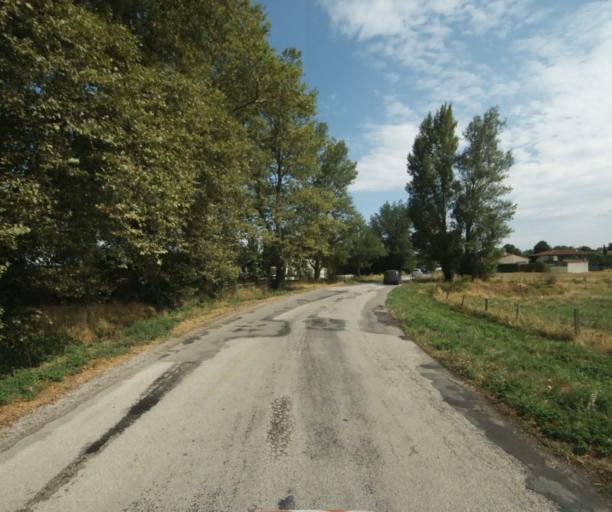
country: FR
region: Midi-Pyrenees
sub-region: Departement de la Haute-Garonne
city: Revel
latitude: 43.4592
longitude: 1.9915
